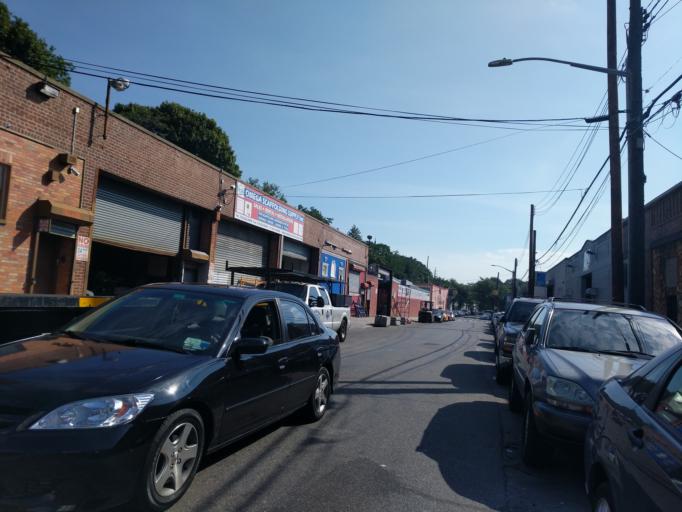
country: US
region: New York
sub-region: Queens County
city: Jamaica
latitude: 40.7002
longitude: -73.8049
